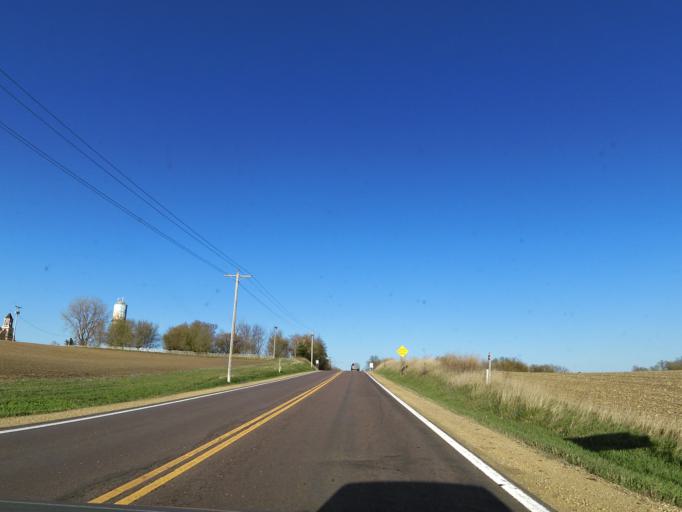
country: US
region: Minnesota
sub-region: Goodhue County
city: Cannon Falls
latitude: 44.6015
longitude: -92.9389
